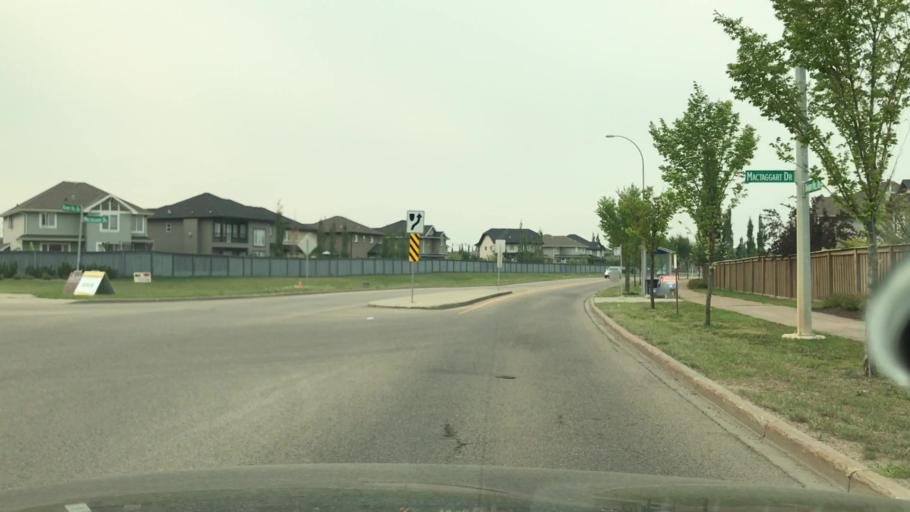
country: CA
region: Alberta
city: Edmonton
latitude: 53.4391
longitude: -113.5660
